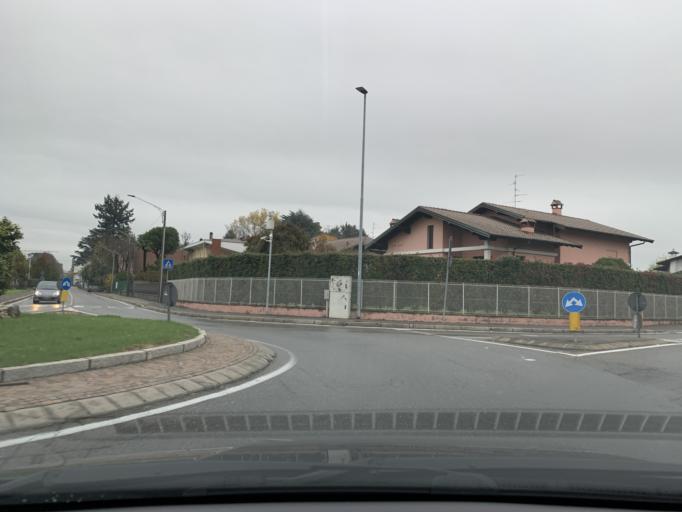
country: IT
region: Lombardy
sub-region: Provincia di Como
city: Rovellasca
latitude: 45.6606
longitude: 9.0535
